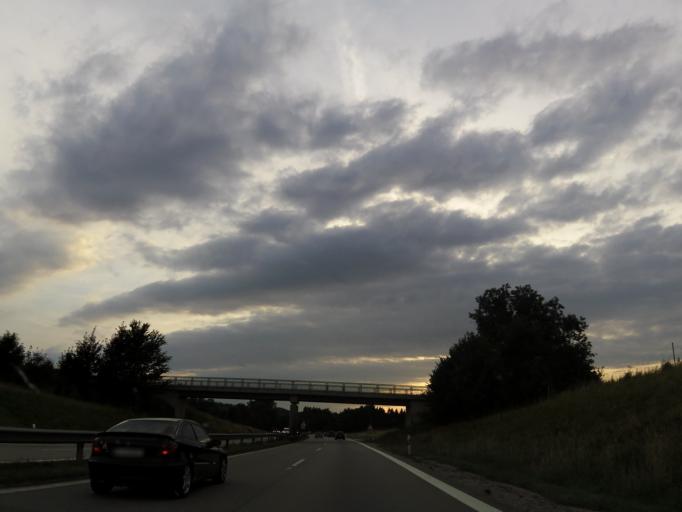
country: DE
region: Bavaria
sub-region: Upper Bavaria
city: Teisendorf
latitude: 47.8271
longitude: 12.7733
